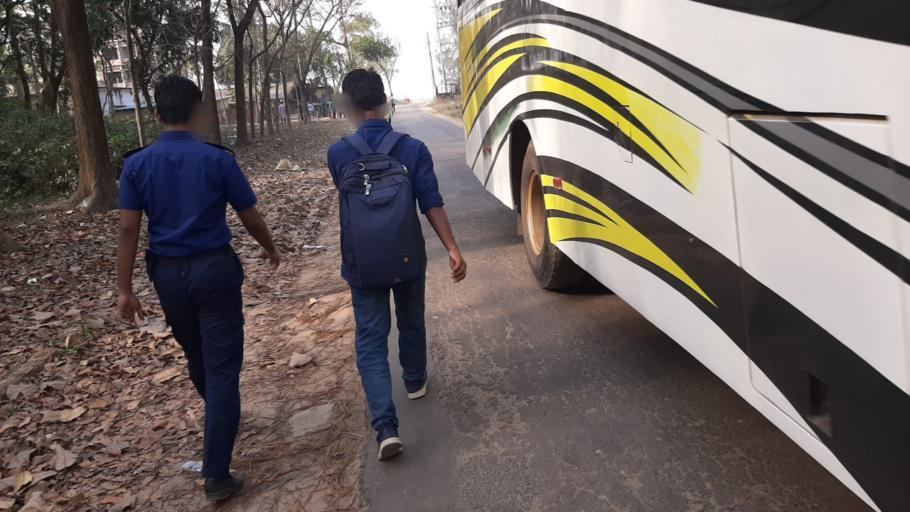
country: BD
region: Chittagong
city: Raojan
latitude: 22.4775
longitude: 91.7909
